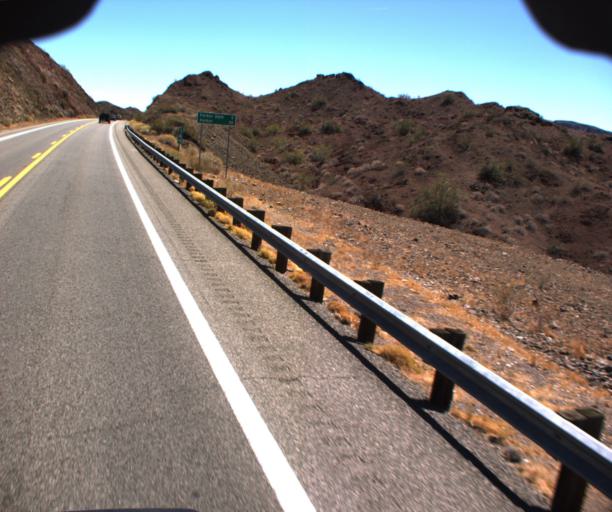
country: US
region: Arizona
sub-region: La Paz County
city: Cienega Springs
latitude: 34.3213
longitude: -114.1191
